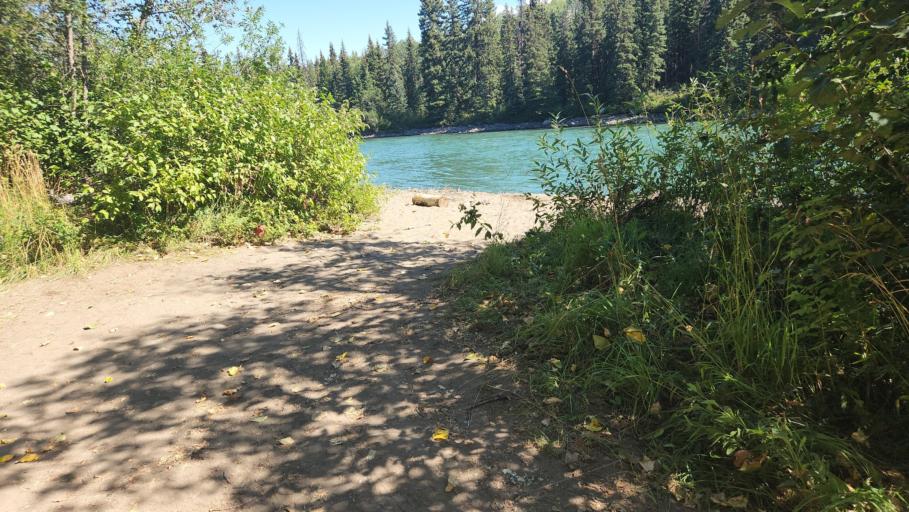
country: CA
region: British Columbia
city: Houston
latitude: 54.3762
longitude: -126.7497
